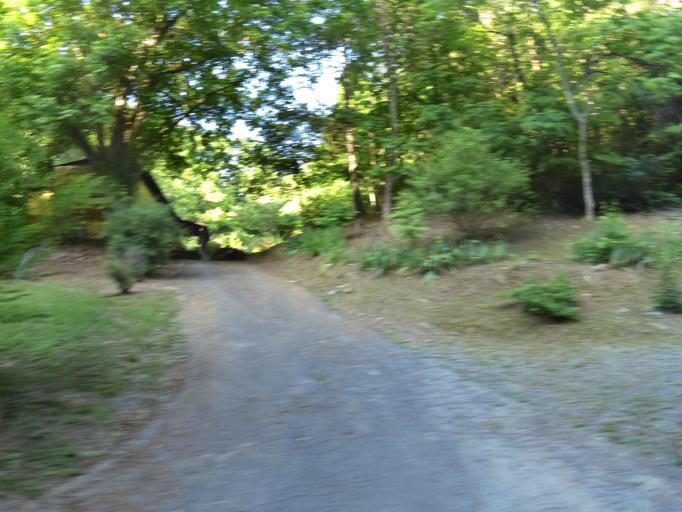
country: US
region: Tennessee
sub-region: Sevier County
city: Sevierville
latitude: 35.8535
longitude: -83.6274
